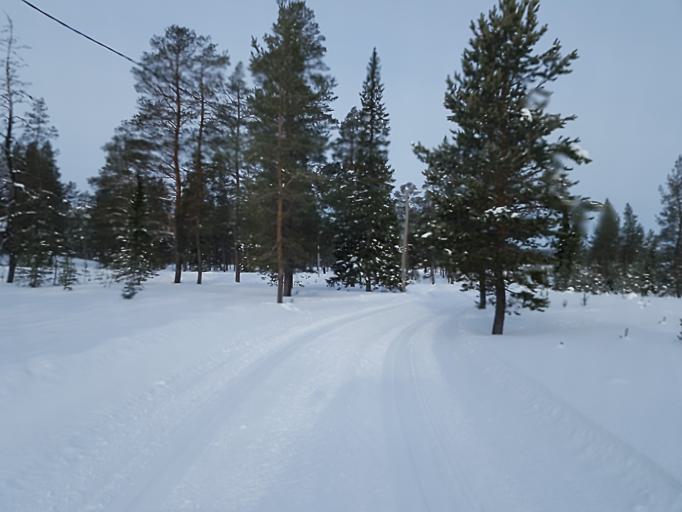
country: FI
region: Lapland
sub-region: Tunturi-Lappi
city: Kolari
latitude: 67.5969
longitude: 24.1537
